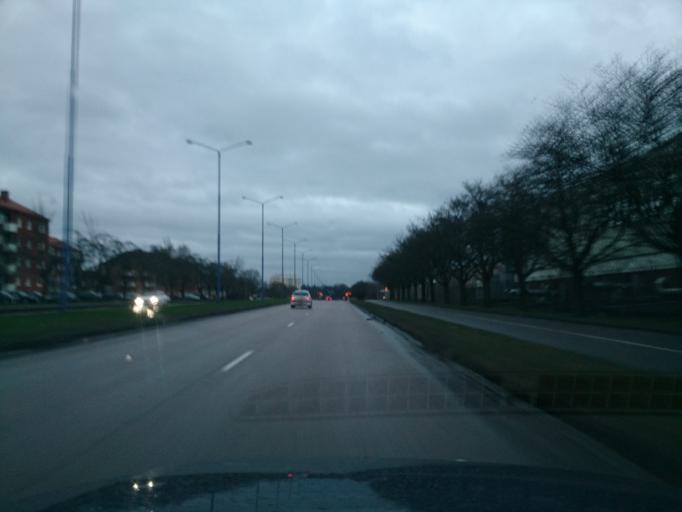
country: SE
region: OEstergoetland
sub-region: Norrkopings Kommun
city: Norrkoping
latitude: 58.5986
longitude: 16.1514
